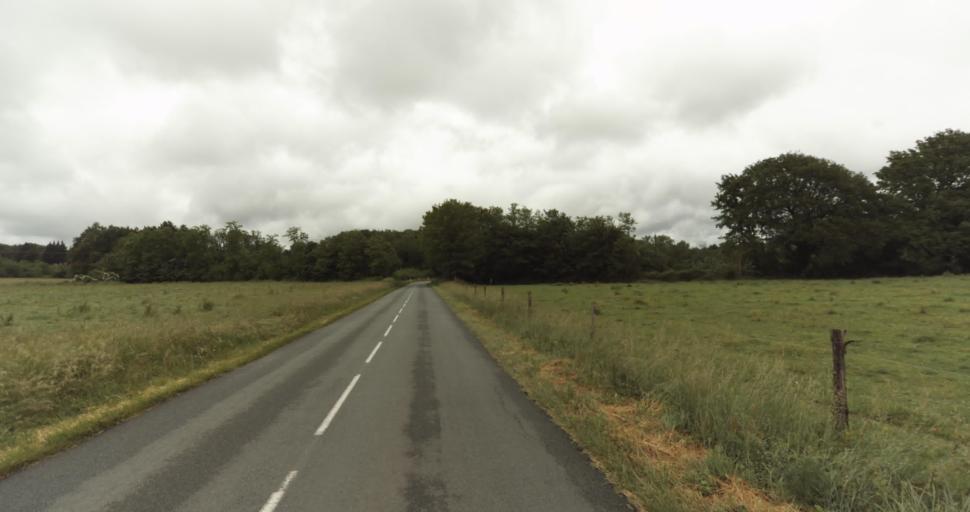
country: FR
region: Aquitaine
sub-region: Departement de la Dordogne
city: Belves
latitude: 44.6908
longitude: 0.9075
